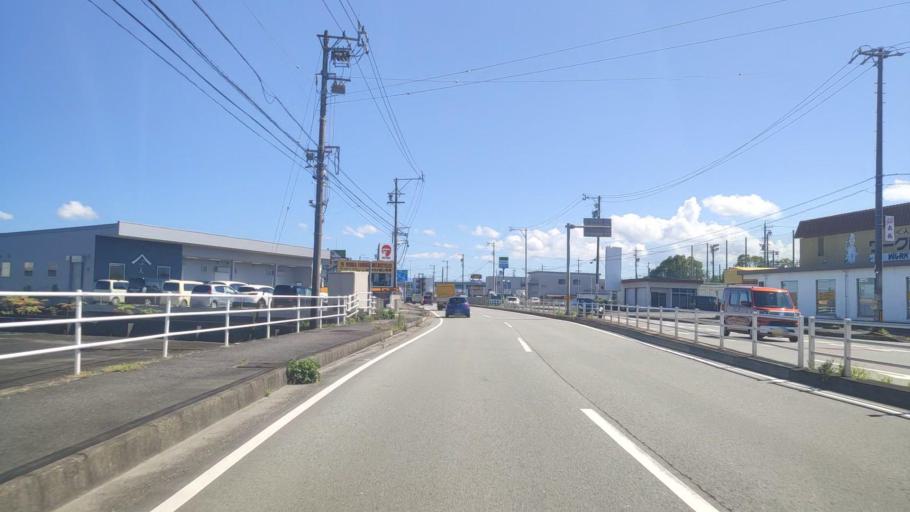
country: JP
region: Mie
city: Hisai-motomachi
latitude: 34.6199
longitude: 136.5155
